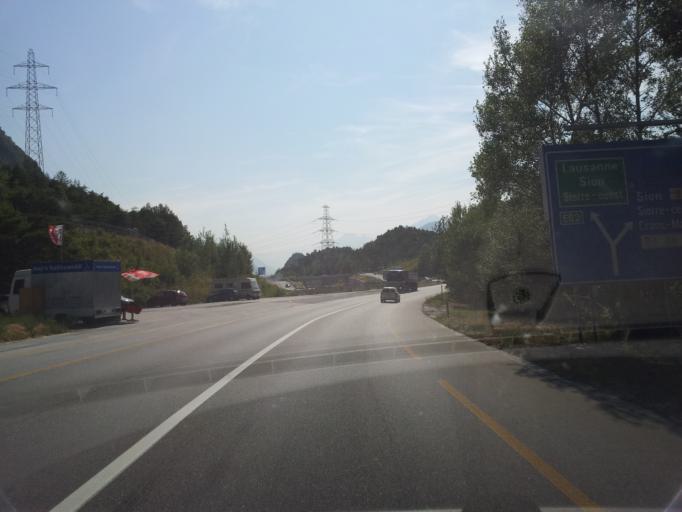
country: CH
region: Valais
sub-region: Leuk District
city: Salgesch
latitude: 46.2902
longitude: 7.5648
